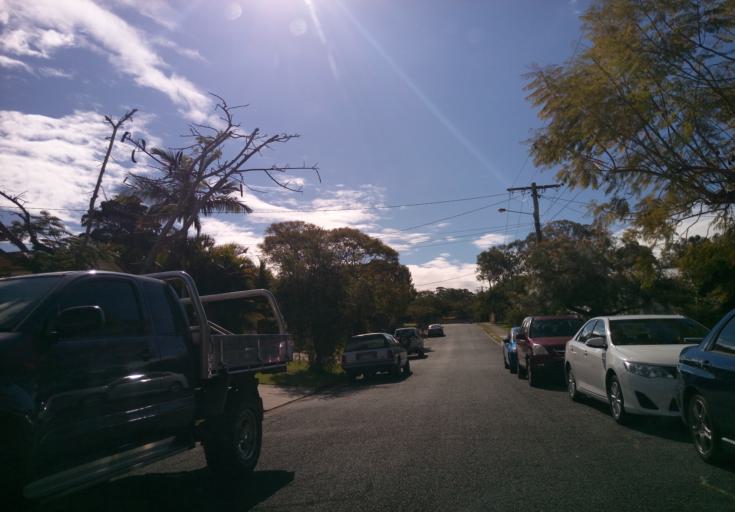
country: AU
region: Queensland
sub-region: Redland
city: Wellington Point
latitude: -27.4918
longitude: 153.2132
